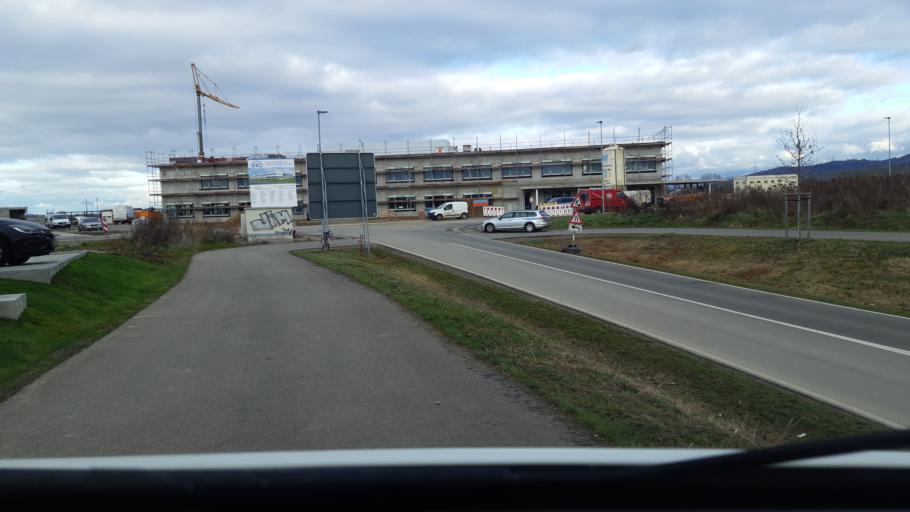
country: DE
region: Baden-Wuerttemberg
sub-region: Freiburg Region
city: Bad Krozingen
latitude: 47.9265
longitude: 7.7022
